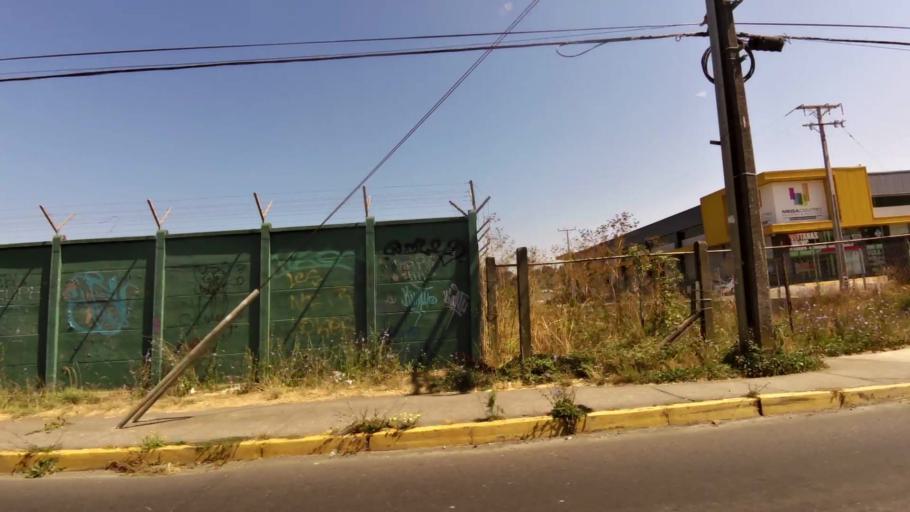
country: CL
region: Biobio
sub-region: Provincia de Concepcion
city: Concepcion
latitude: -36.8145
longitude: -73.0640
